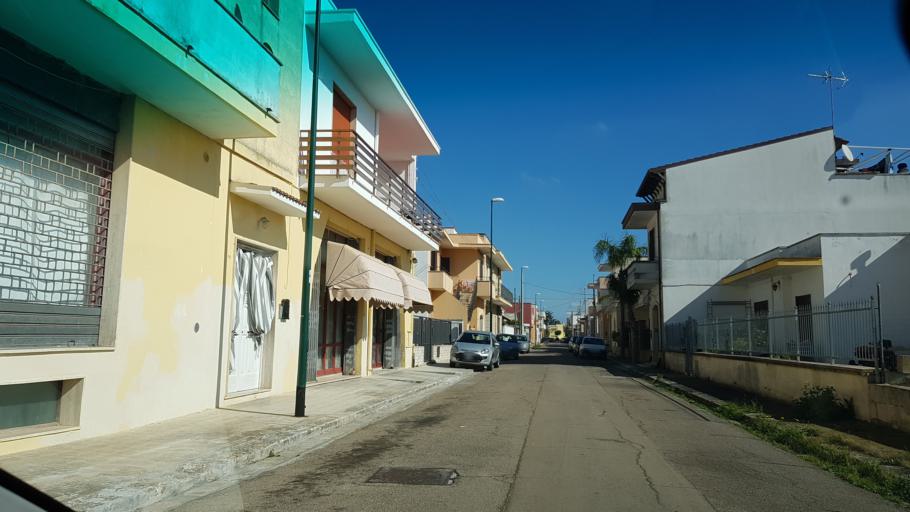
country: IT
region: Apulia
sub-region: Provincia di Lecce
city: Campi Salentina
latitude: 40.3931
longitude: 18.0098
